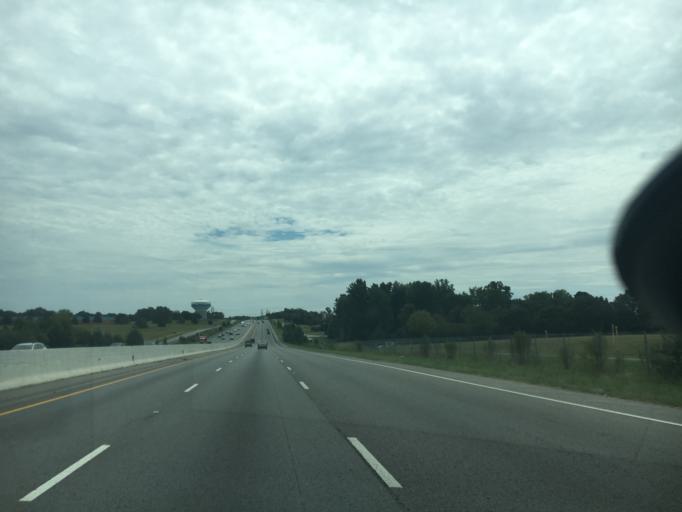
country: US
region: South Carolina
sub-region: Greenville County
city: Simpsonville
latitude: 34.7012
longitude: -82.2360
